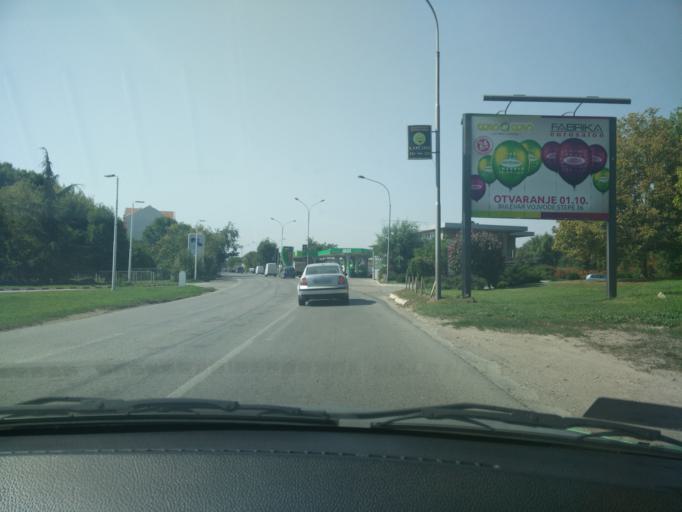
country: RS
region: Autonomna Pokrajina Vojvodina
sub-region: Juznobacki Okrug
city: Novi Sad
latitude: 45.2674
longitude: 19.8492
